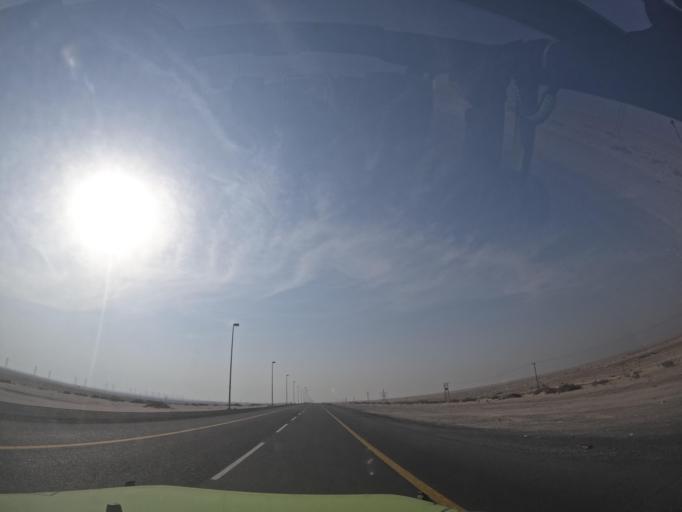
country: AE
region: Dubai
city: Dubai
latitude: 24.7605
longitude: 55.0979
